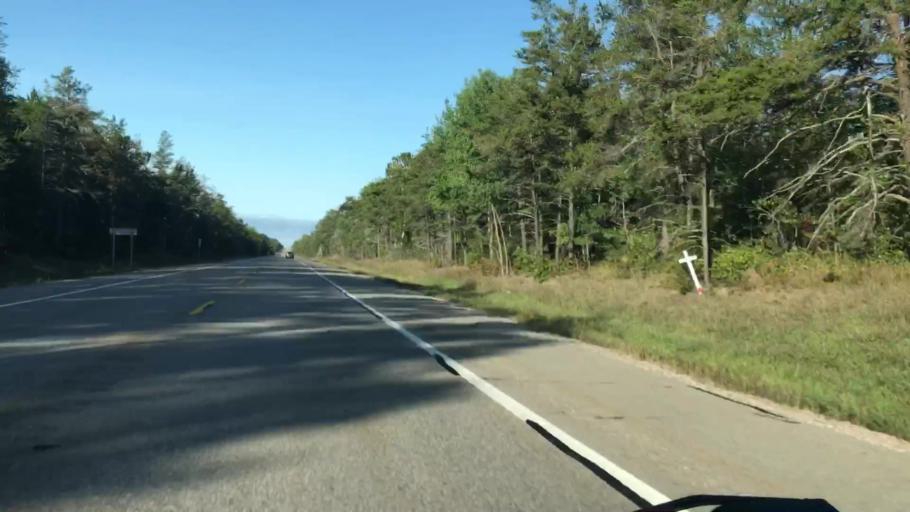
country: US
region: Michigan
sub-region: Chippewa County
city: Sault Ste. Marie
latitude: 46.3692
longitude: -84.7396
